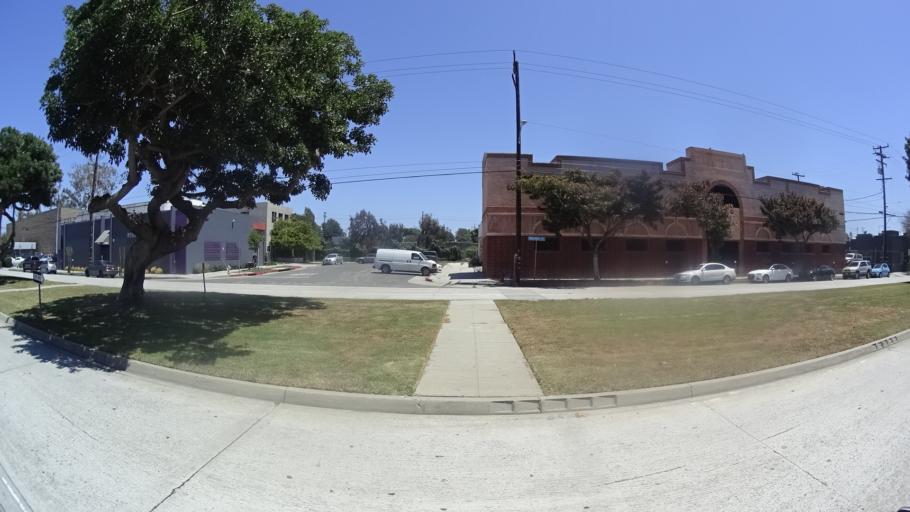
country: US
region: California
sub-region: Los Angeles County
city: Santa Monica
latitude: 34.0189
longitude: -118.4816
